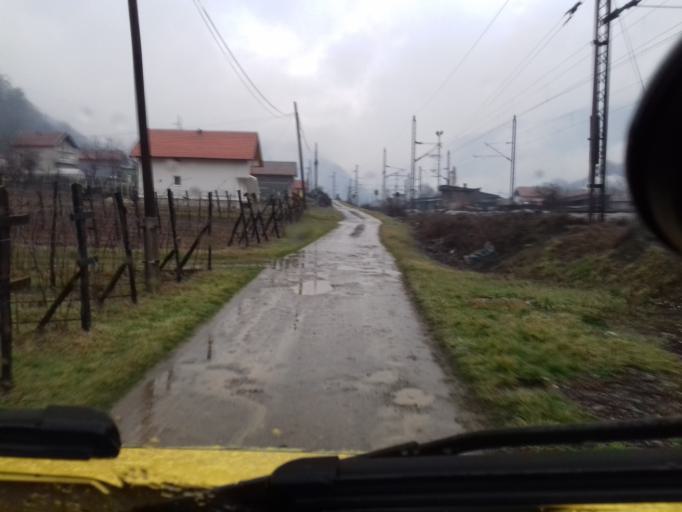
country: BA
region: Federation of Bosnia and Herzegovina
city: Zeljezno Polje
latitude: 44.3229
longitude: 17.9057
